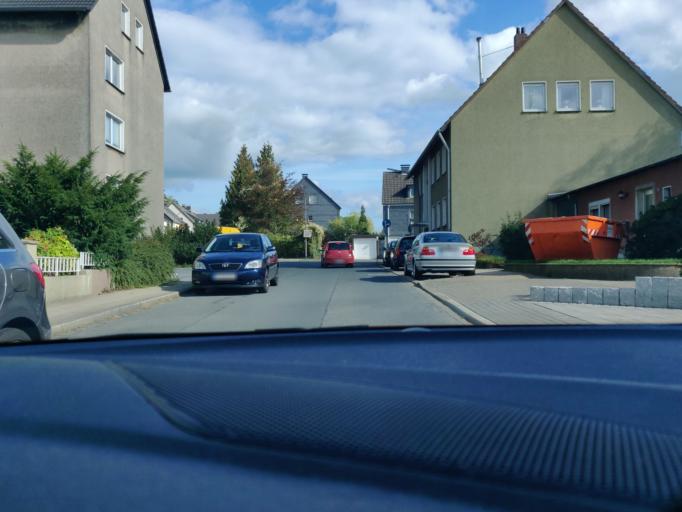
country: DE
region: North Rhine-Westphalia
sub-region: Regierungsbezirk Dusseldorf
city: Velbert
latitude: 51.3298
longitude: 7.0274
